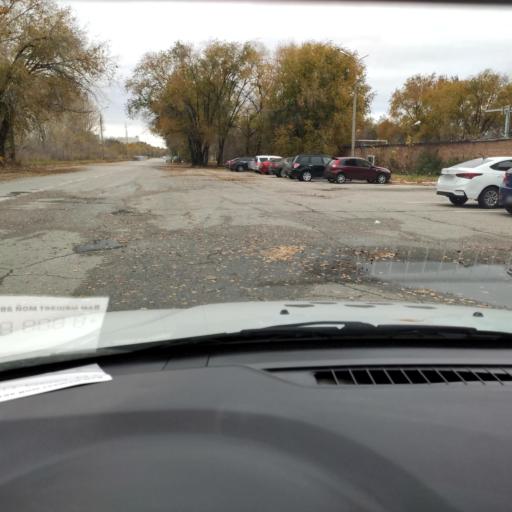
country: RU
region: Samara
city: Tol'yatti
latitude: 53.5531
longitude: 49.2993
